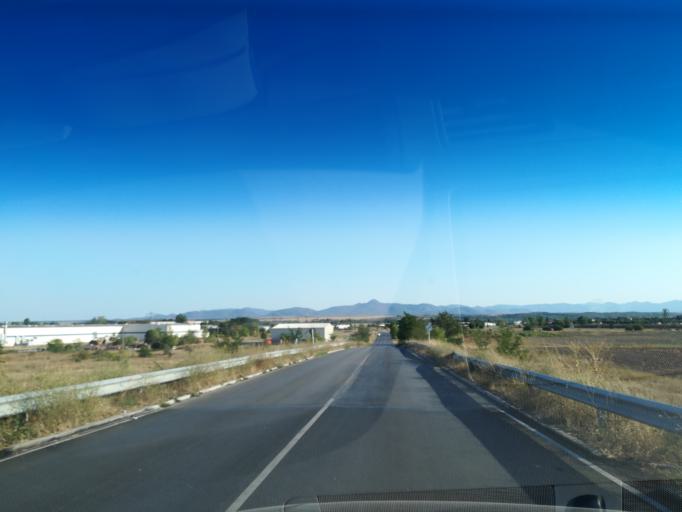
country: BG
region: Stara Zagora
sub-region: Obshtina Chirpan
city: Chirpan
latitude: 42.0981
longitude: 25.2104
